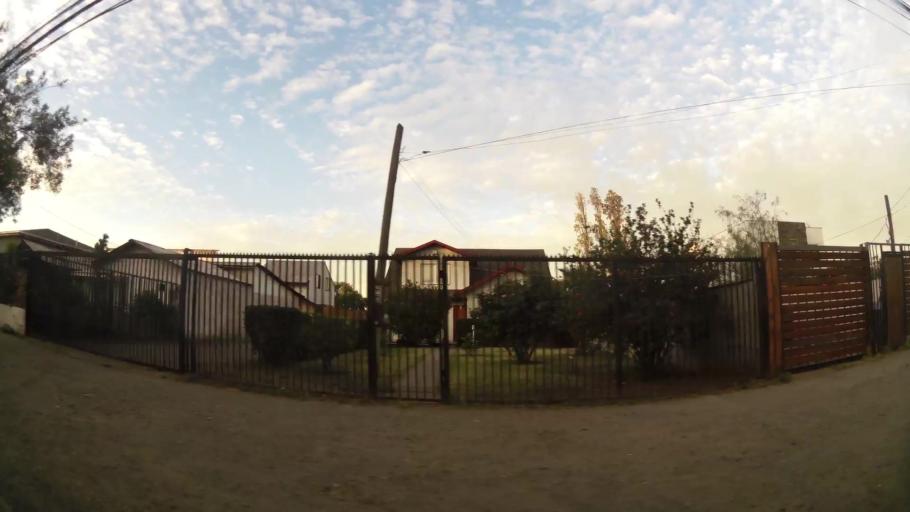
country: CL
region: Santiago Metropolitan
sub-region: Provincia de Maipo
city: San Bernardo
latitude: -33.6198
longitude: -70.6916
